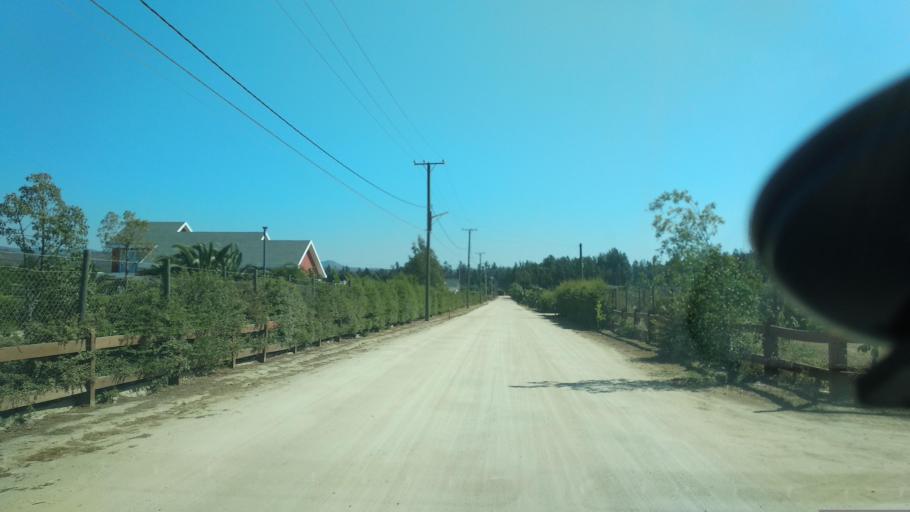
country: CL
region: Valparaiso
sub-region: Provincia de Marga Marga
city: Limache
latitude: -32.9712
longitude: -71.3084
